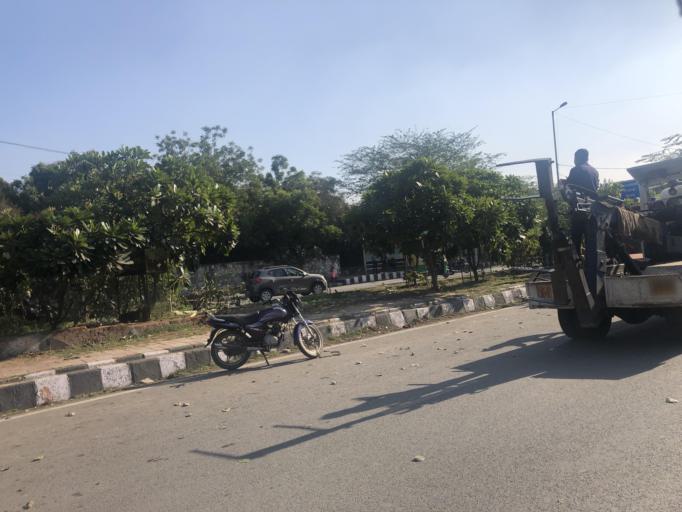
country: IN
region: NCT
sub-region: Central Delhi
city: Karol Bagh
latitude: 28.5526
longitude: 77.1655
